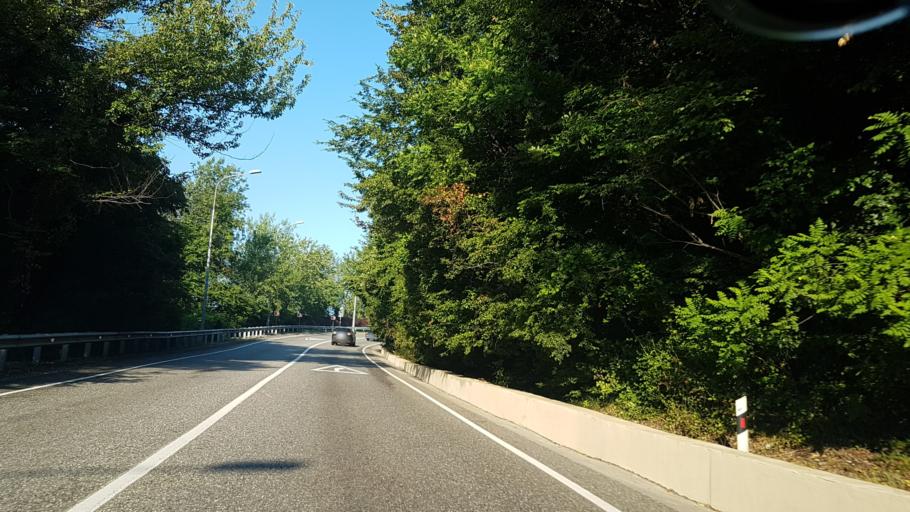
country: RU
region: Krasnodarskiy
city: Vardane
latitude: 43.7528
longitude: 39.5292
